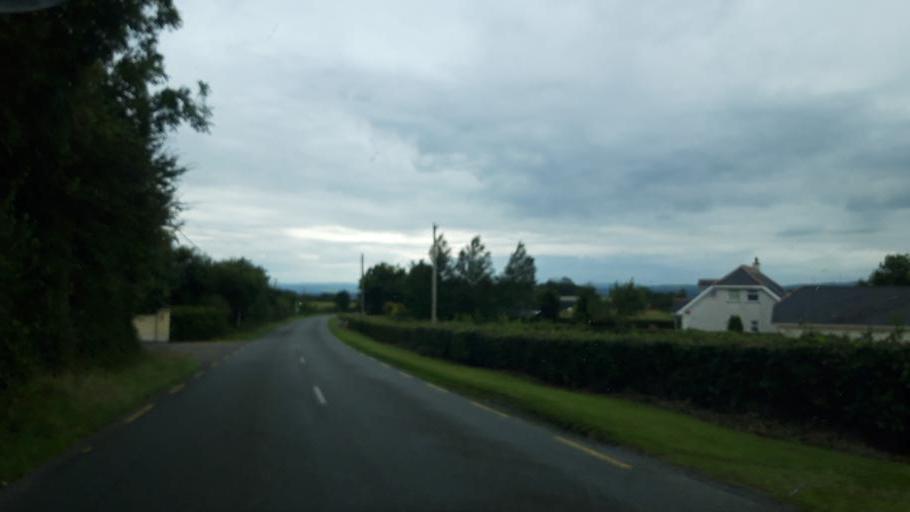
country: IE
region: Leinster
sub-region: Kilkenny
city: Ballyragget
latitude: 52.7991
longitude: -7.3071
